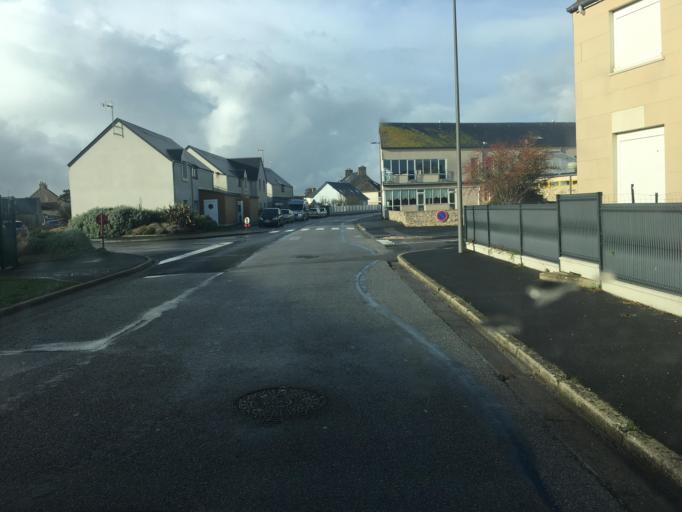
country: FR
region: Lower Normandy
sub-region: Departement de la Manche
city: Saint-Vaast-la-Hougue
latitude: 49.5861
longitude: -1.2715
